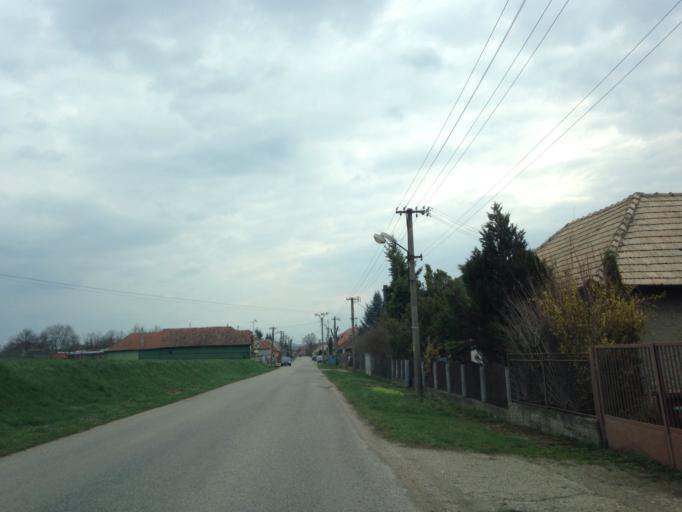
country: SK
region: Nitriansky
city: Svodin
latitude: 47.9088
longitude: 18.4109
